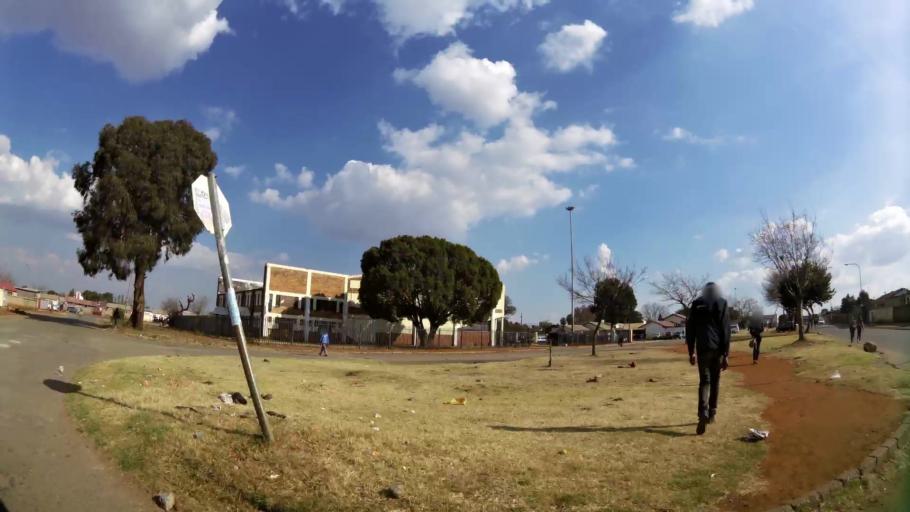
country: ZA
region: Gauteng
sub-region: City of Johannesburg Metropolitan Municipality
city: Soweto
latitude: -26.2222
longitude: 27.8663
